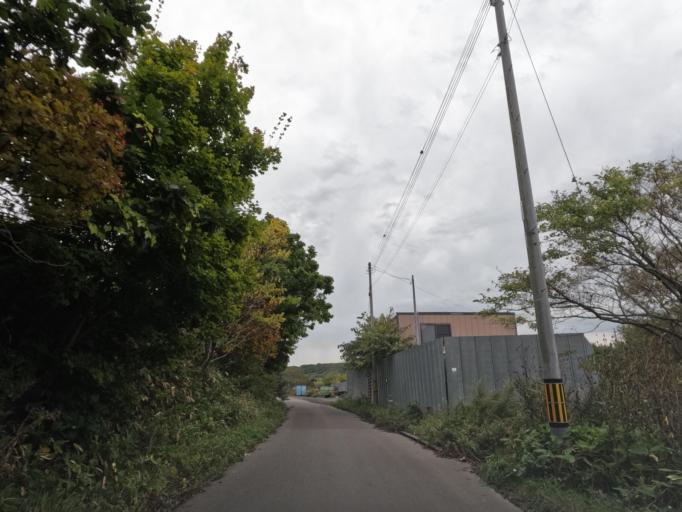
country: JP
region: Hokkaido
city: Date
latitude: 42.4004
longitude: 140.9108
